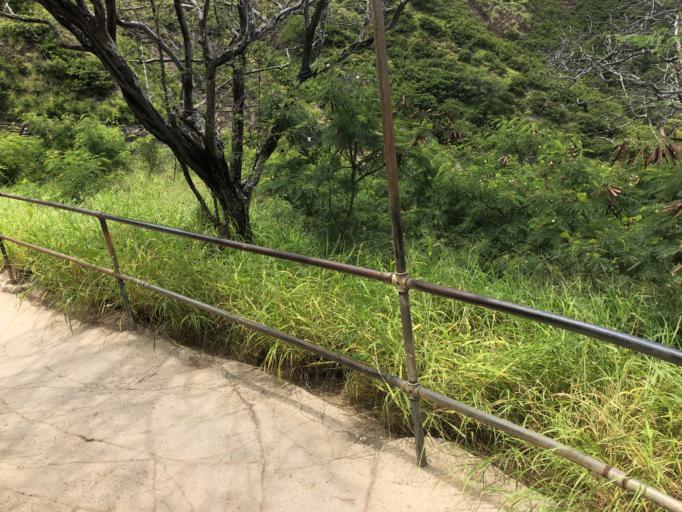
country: US
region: Hawaii
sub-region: Honolulu County
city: Honolulu
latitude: 21.2613
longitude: -157.8103
